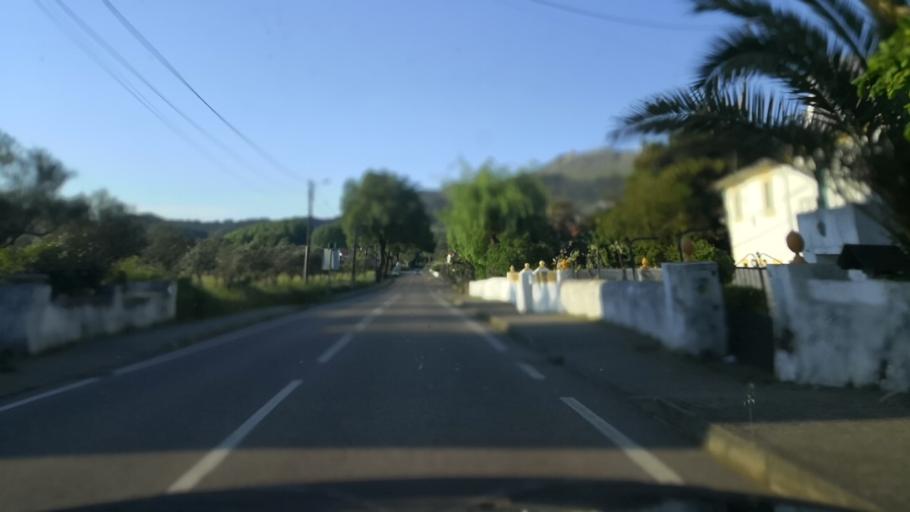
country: PT
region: Portalegre
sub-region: Marvao
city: Marvao
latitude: 39.3757
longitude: -7.3887
